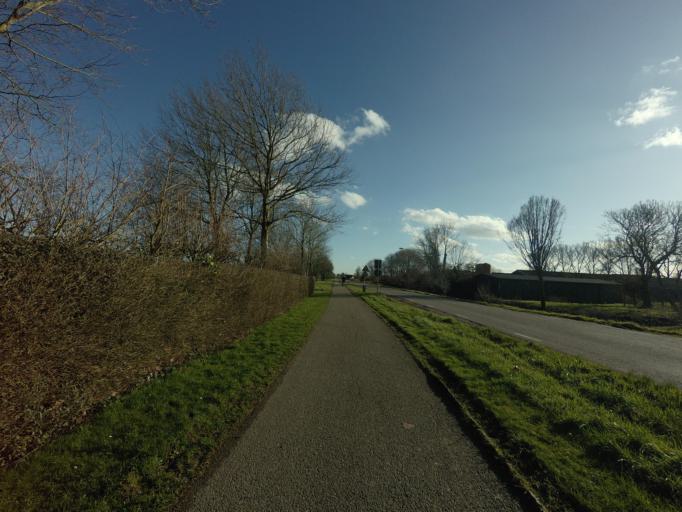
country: NL
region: Utrecht
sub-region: Gemeente IJsselstein
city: IJsselstein
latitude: 52.0005
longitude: 5.0491
